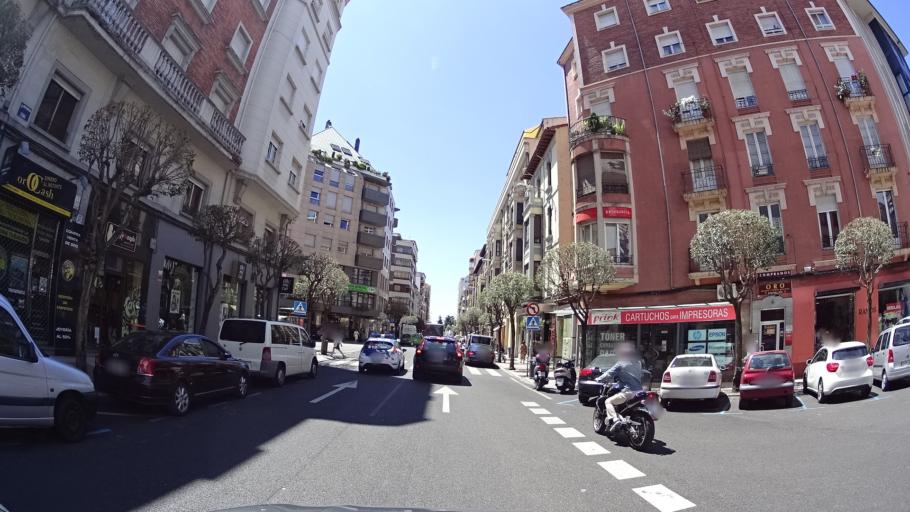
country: ES
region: Castille and Leon
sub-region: Provincia de Leon
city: Leon
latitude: 42.5985
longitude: -5.5765
